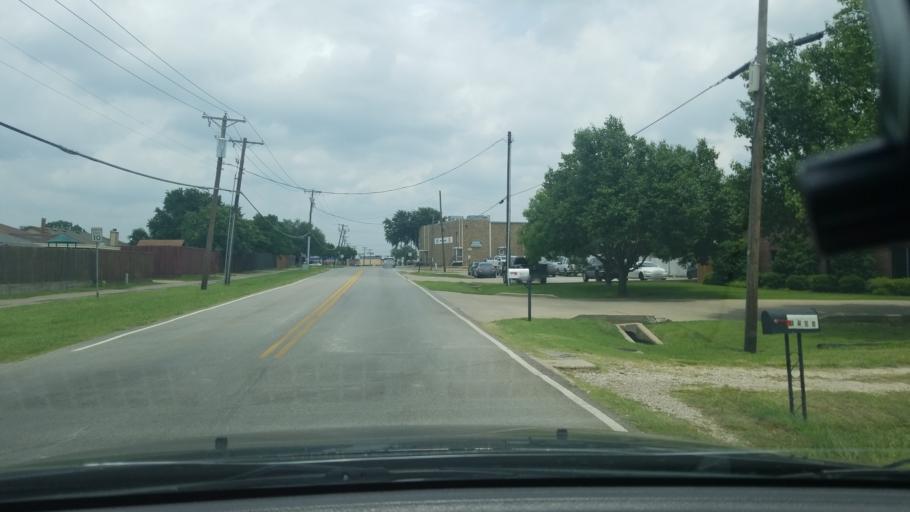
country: US
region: Texas
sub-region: Dallas County
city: Mesquite
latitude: 32.7960
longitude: -96.6144
